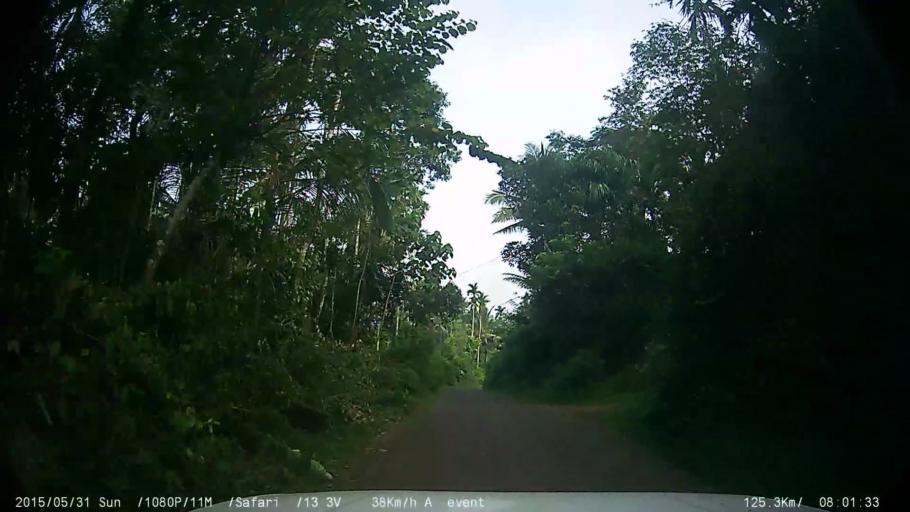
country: IN
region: Kerala
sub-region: Wayanad
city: Kalpetta
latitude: 11.6330
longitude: 76.0462
